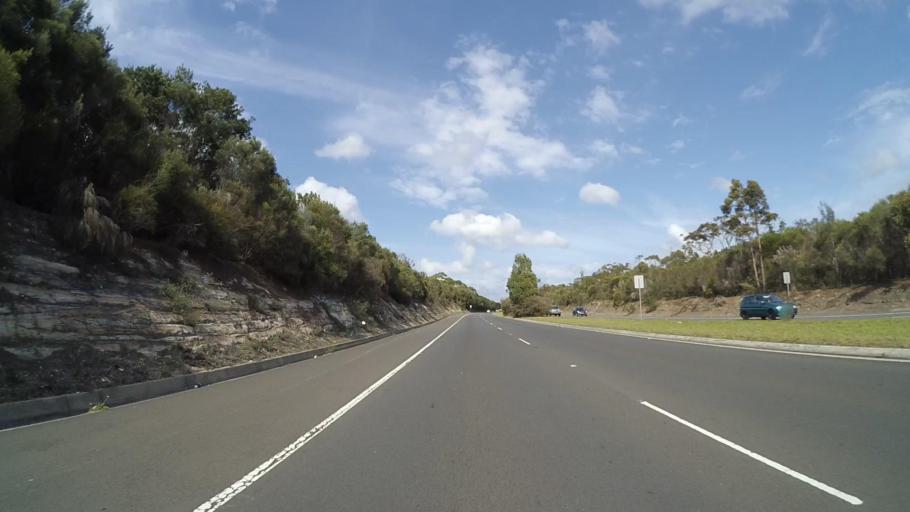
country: AU
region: New South Wales
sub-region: Sutherland Shire
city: Loftus
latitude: -34.0571
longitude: 151.0397
